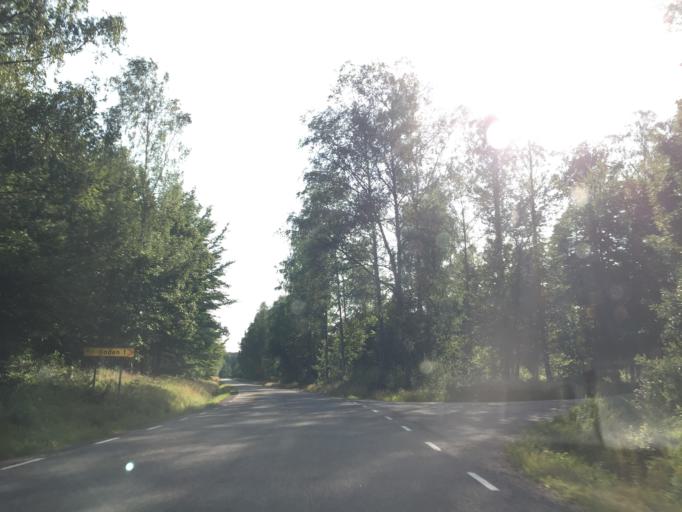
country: SE
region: Vaestra Goetaland
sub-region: Trollhattan
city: Sjuntorp
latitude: 58.2333
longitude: 12.1688
